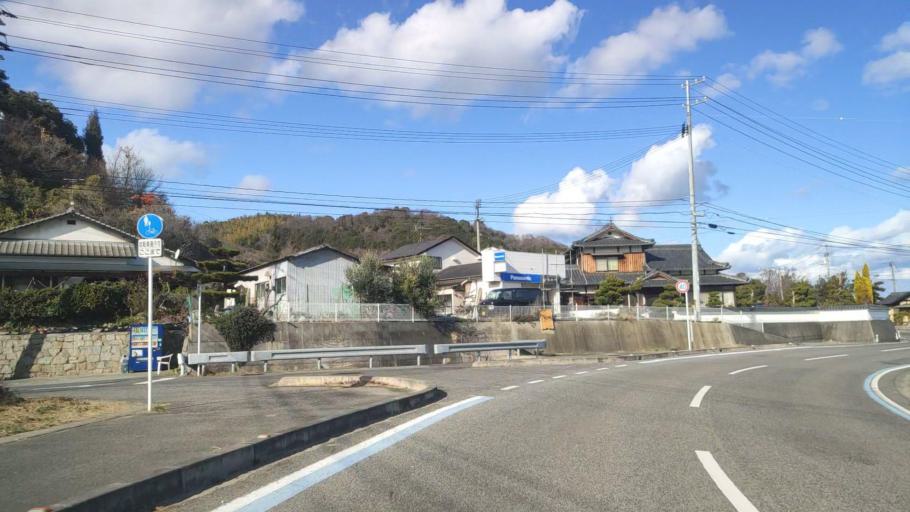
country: JP
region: Hiroshima
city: Innoshima
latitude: 34.2181
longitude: 133.1064
